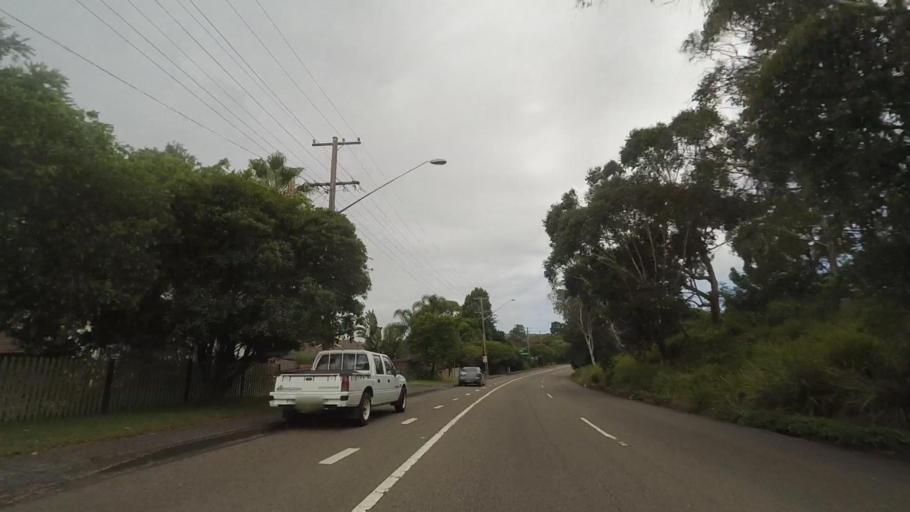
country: AU
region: New South Wales
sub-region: Wyong Shire
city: Berkeley Vale
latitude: -33.3549
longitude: 151.4392
